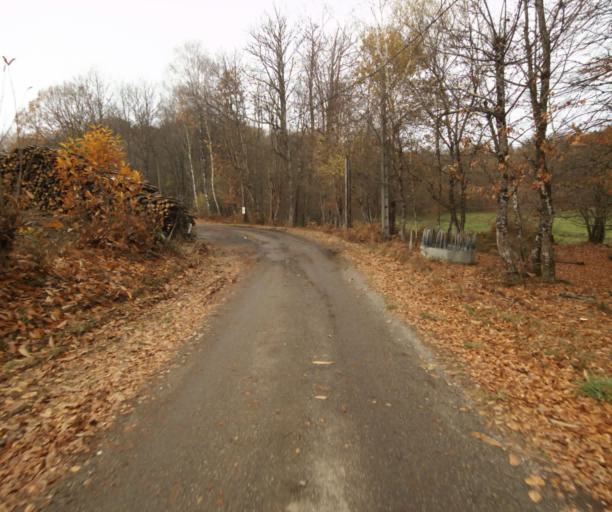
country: FR
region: Limousin
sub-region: Departement de la Correze
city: Sainte-Fortunade
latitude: 45.1853
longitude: 1.7655
